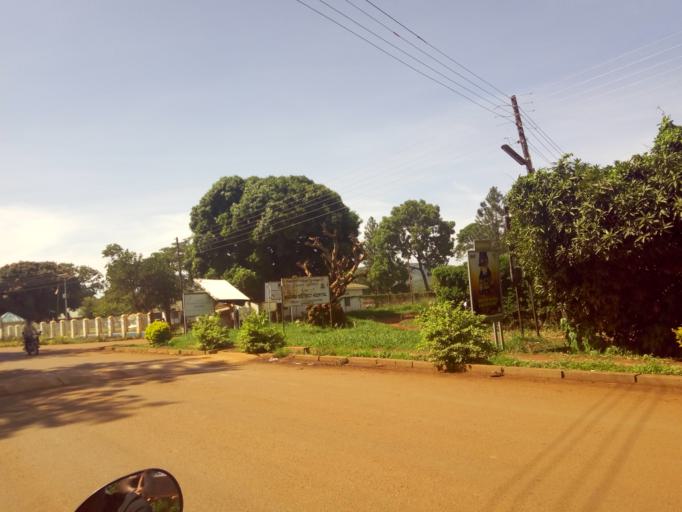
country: UG
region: Western Region
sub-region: Masindi District
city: Masindi
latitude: 1.6858
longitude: 31.7178
